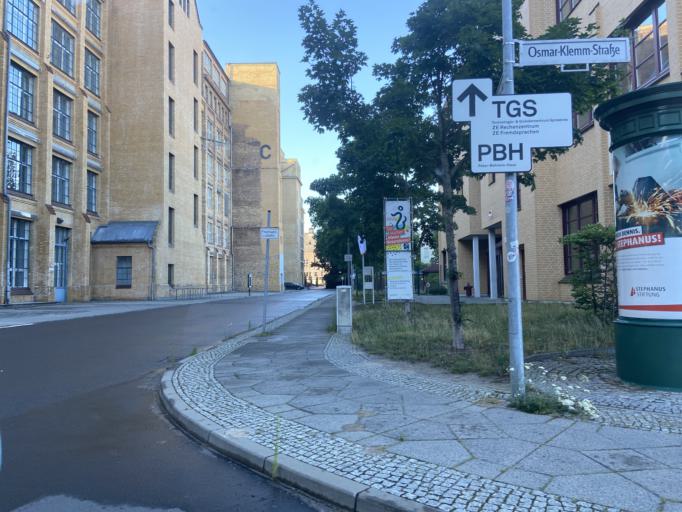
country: DE
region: Berlin
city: Oberschoneweide
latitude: 52.4561
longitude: 13.5263
